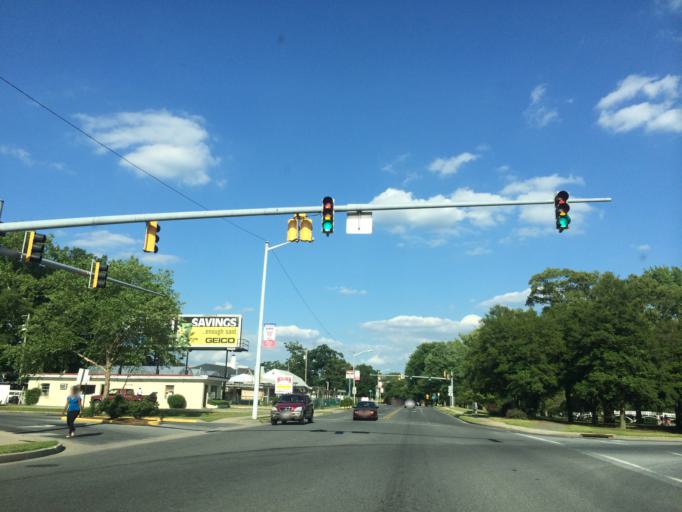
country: US
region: Maryland
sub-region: Wicomico County
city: Salisbury
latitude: 38.3655
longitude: -75.5931
